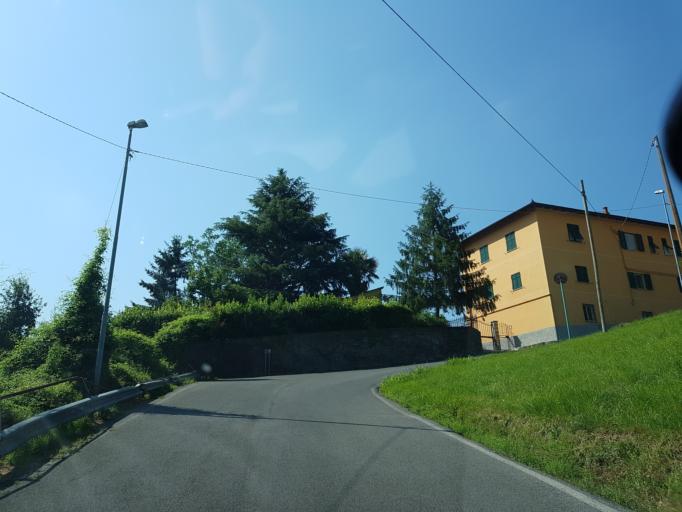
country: IT
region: Liguria
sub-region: Provincia di Genova
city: Pedemonte
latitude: 44.5026
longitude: 8.9196
